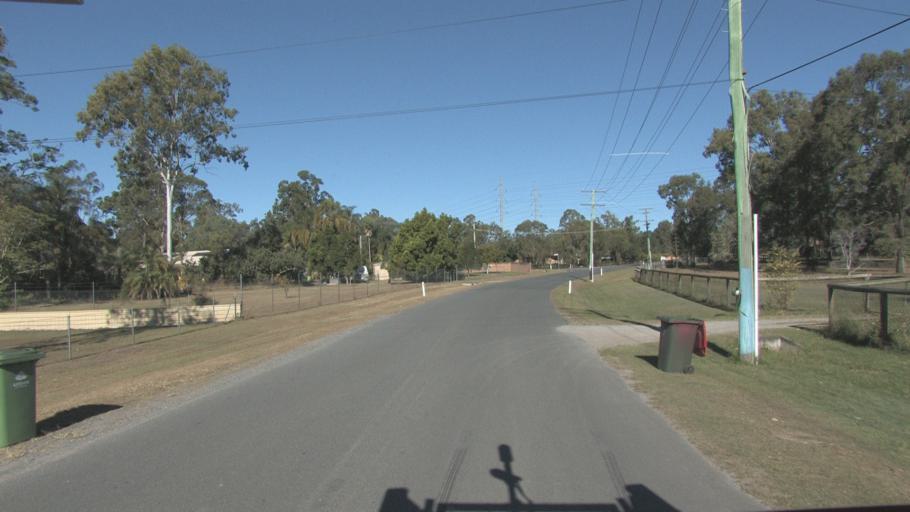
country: AU
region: Queensland
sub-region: Logan
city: Park Ridge South
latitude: -27.7315
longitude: 153.0214
